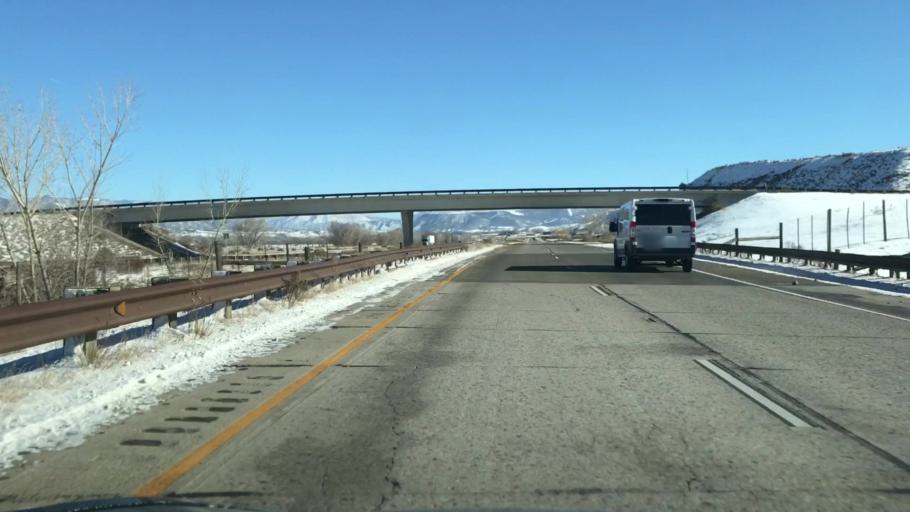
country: US
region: Colorado
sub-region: Garfield County
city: Silt
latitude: 39.5319
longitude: -107.7141
